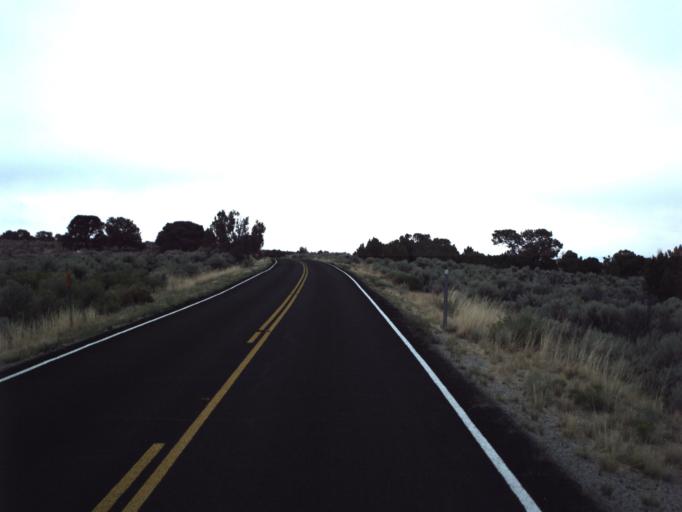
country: US
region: Utah
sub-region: Carbon County
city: East Carbon City
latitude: 39.4686
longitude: -110.3961
